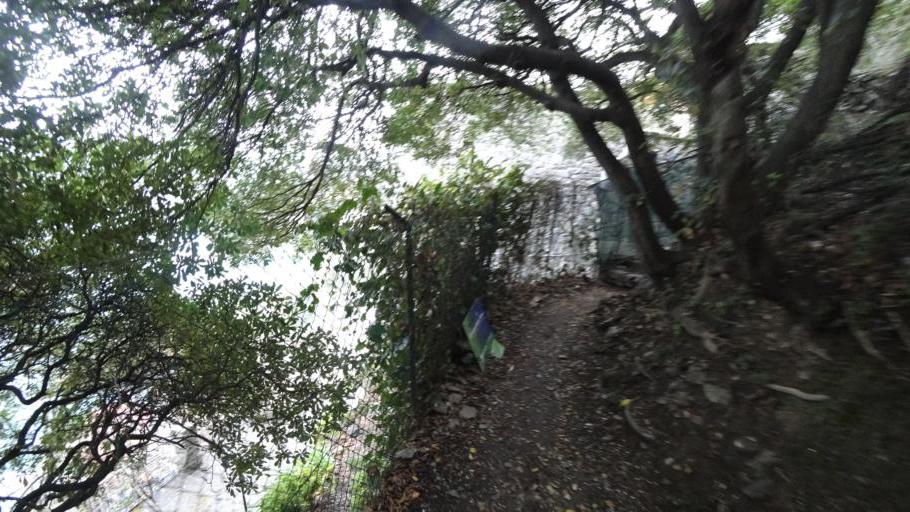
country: IT
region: Liguria
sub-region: Provincia di La Spezia
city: Monterosso al Mare
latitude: 44.1446
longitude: 9.6589
